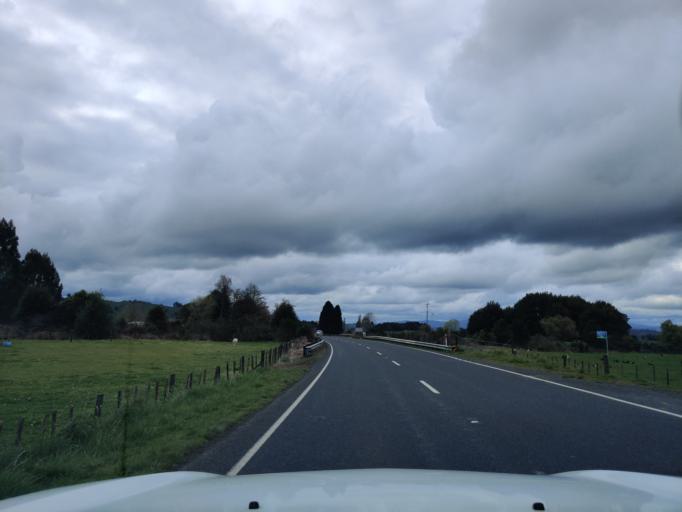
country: NZ
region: Waikato
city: Turangi
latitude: -38.9913
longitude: 175.3788
